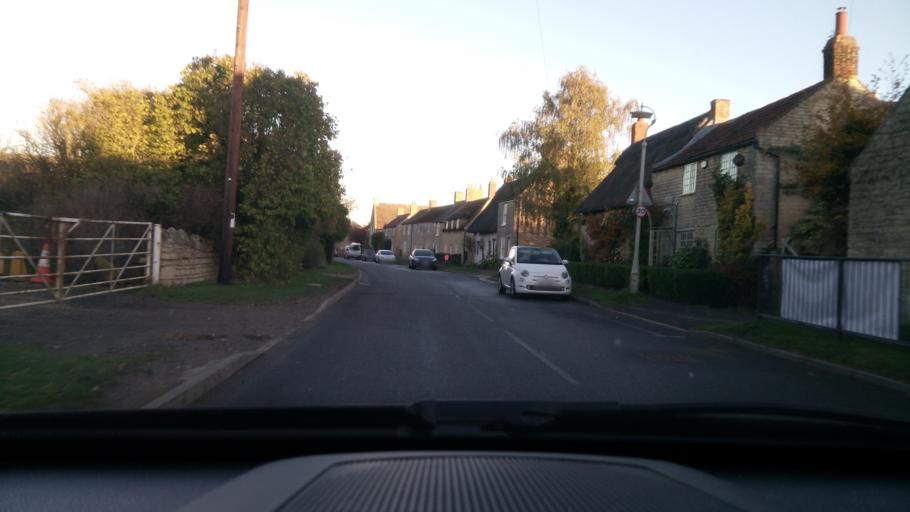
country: GB
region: England
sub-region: Peterborough
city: Helpston
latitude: 52.6351
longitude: -0.3475
